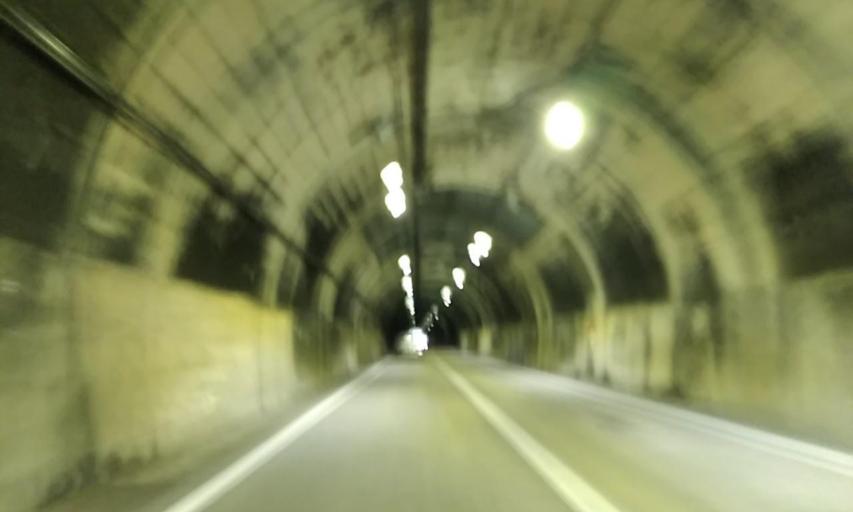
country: JP
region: Mie
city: Ise
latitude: 34.4110
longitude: 136.7645
